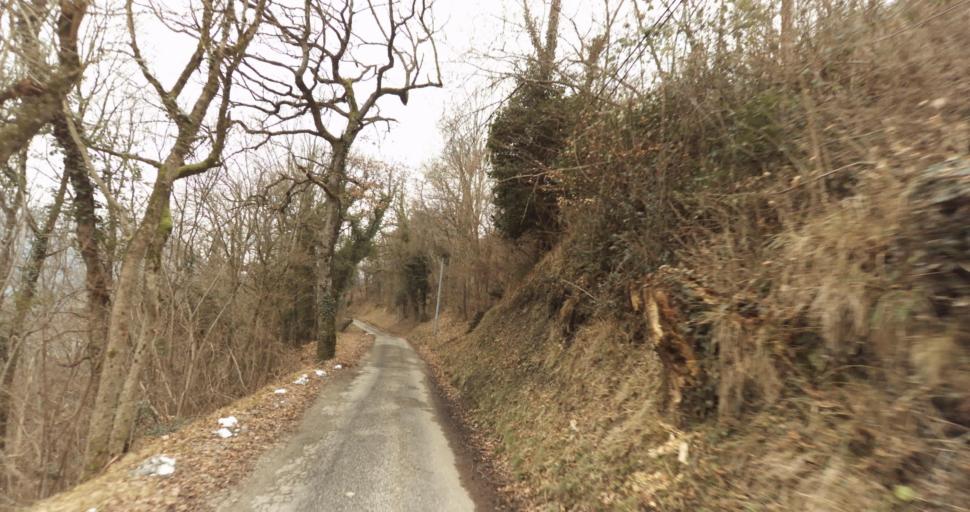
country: FR
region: Rhone-Alpes
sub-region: Departement de l'Isere
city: Saint-Georges-de-Commiers
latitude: 45.0180
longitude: 5.6847
